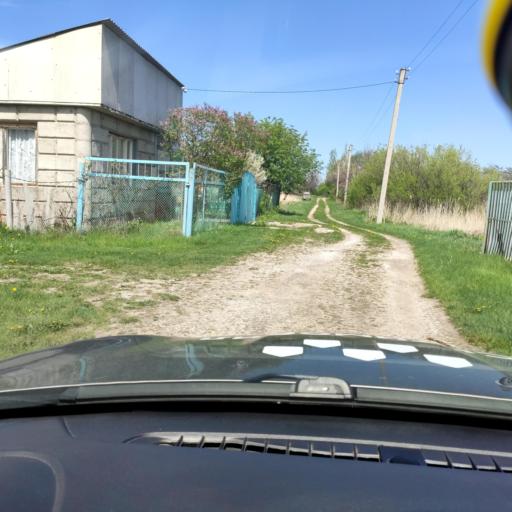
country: RU
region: Samara
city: Tol'yatti
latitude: 53.7017
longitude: 49.4340
